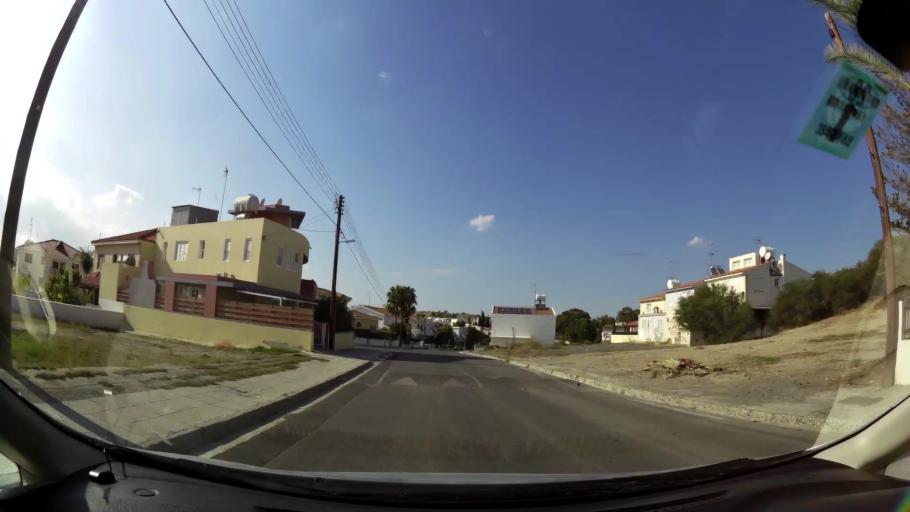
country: CY
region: Lefkosia
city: Nicosia
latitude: 35.1542
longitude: 33.3058
